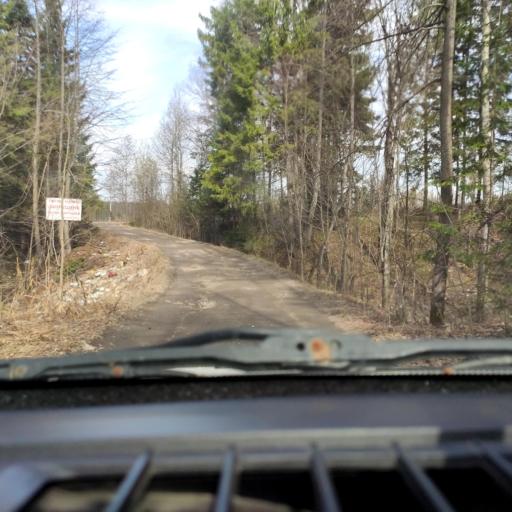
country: RU
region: Perm
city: Kultayevo
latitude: 57.8227
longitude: 55.7912
